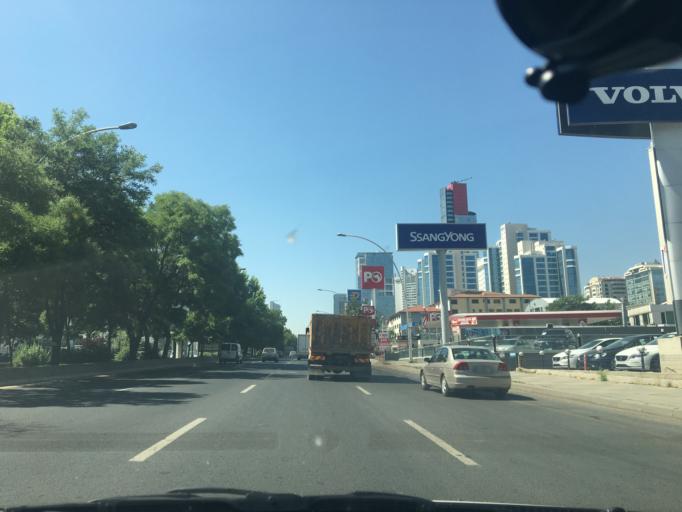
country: TR
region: Ankara
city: Ankara
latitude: 39.8961
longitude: 32.8132
